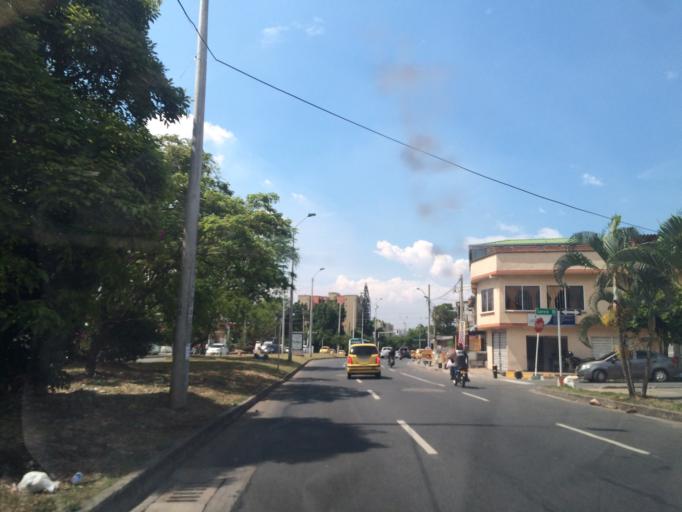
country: CO
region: Valle del Cauca
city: Cali
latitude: 3.4049
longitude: -76.5273
